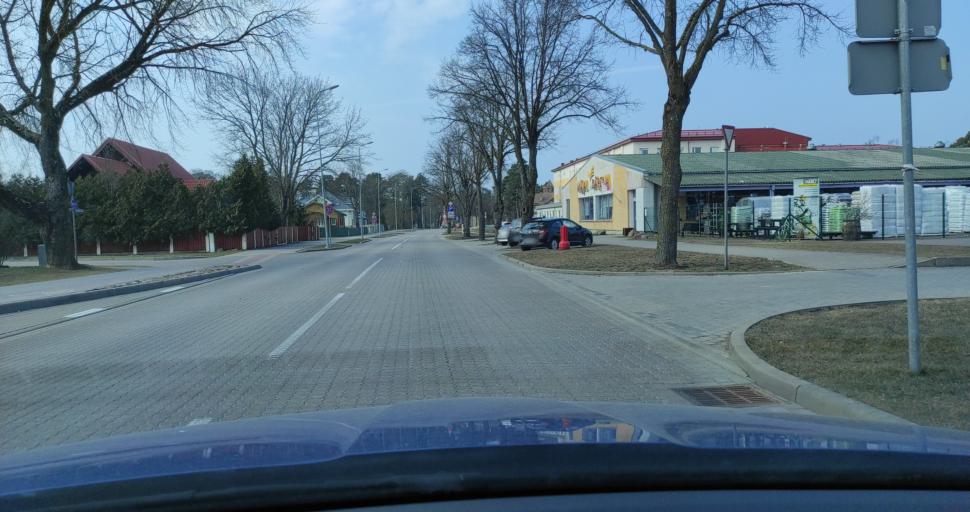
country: LV
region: Ventspils
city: Ventspils
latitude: 57.3858
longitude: 21.5458
